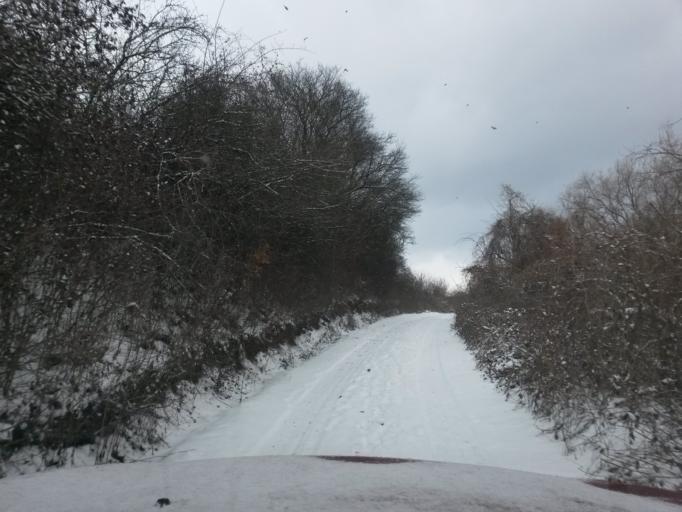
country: HU
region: Borsod-Abauj-Zemplen
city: Gonc
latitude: 48.5939
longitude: 21.3797
